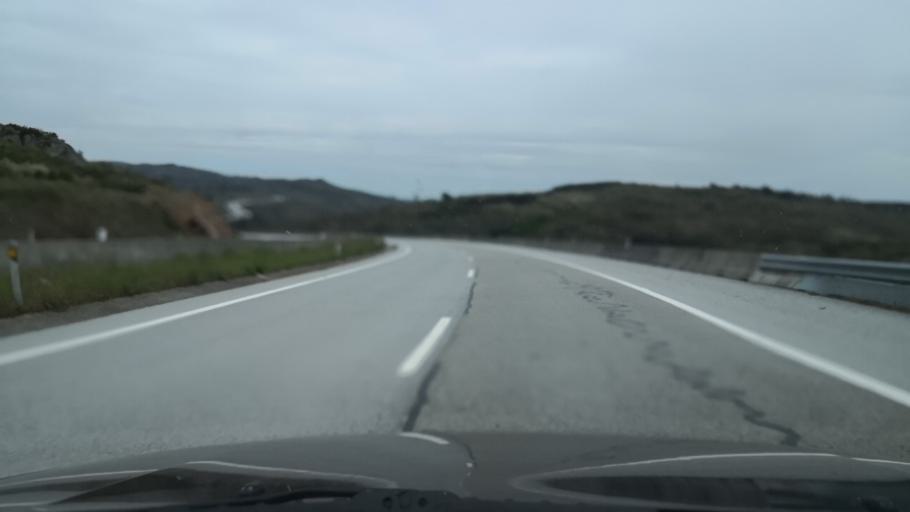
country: PT
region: Guarda
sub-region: Fornos de Algodres
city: Fornos de Algodres
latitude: 40.6236
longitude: -7.4829
